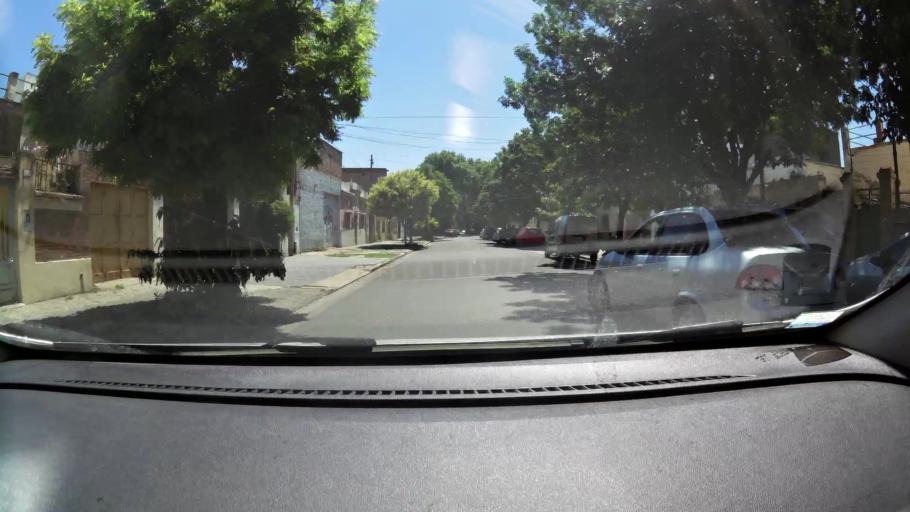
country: AR
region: Santa Fe
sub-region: Departamento de Rosario
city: Rosario
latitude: -32.9342
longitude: -60.6728
